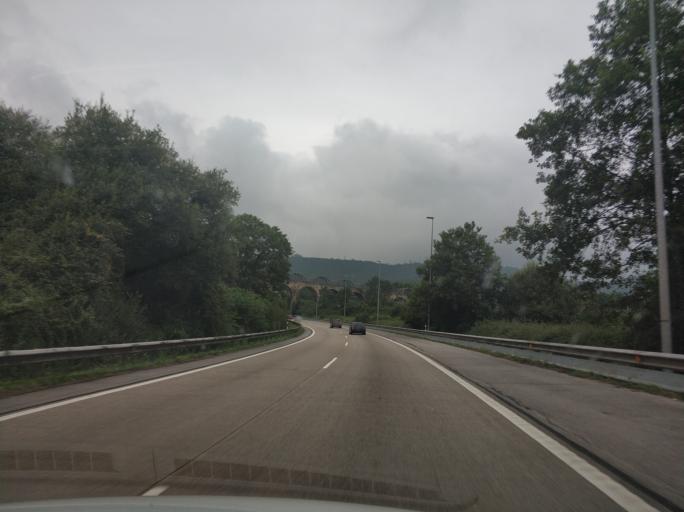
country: ES
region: Asturias
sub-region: Province of Asturias
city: Corvera de Asturias
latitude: 43.4993
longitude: -5.7854
